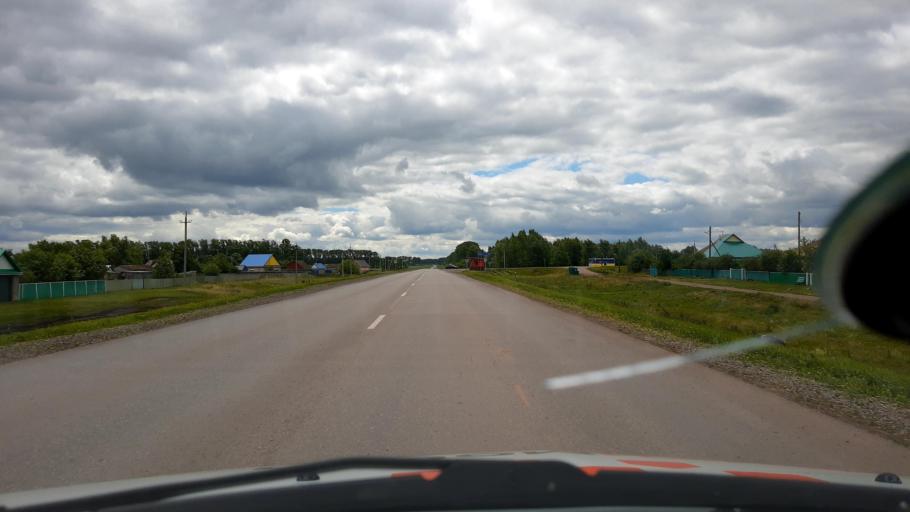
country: RU
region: Bashkortostan
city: Buzdyak
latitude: 54.6858
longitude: 54.5545
